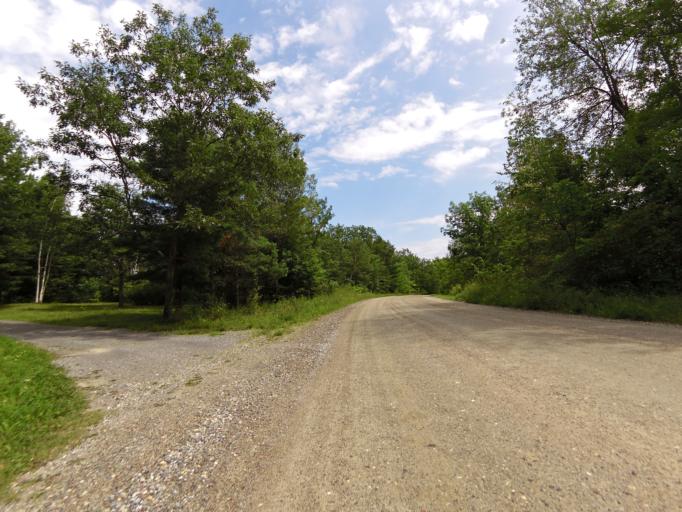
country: CA
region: Ontario
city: Perth
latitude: 44.7900
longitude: -76.6338
